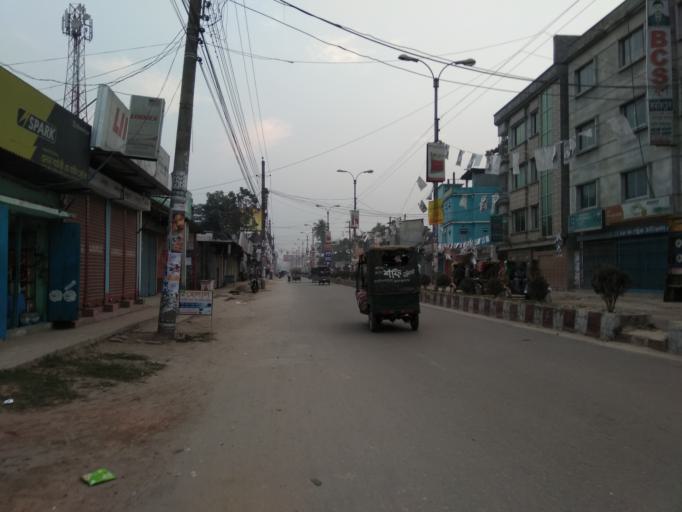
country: BD
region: Rangpur Division
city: Rangpur
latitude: 25.7375
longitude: 89.2548
